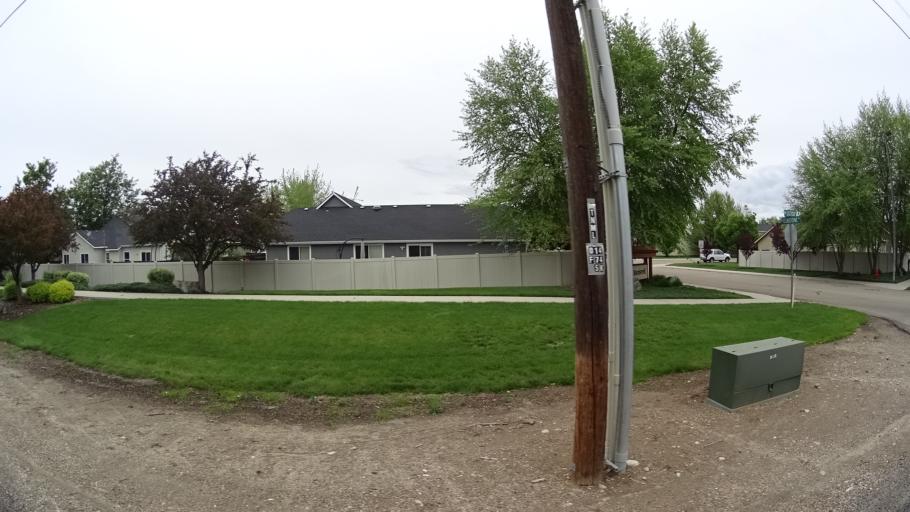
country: US
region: Idaho
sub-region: Ada County
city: Meridian
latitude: 43.6341
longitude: -116.4554
